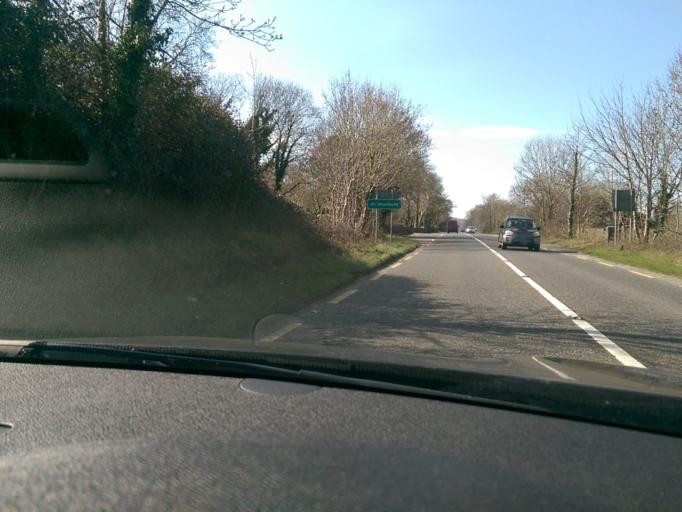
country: IE
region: Connaught
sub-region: County Galway
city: Bearna
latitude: 53.3041
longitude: -9.1092
